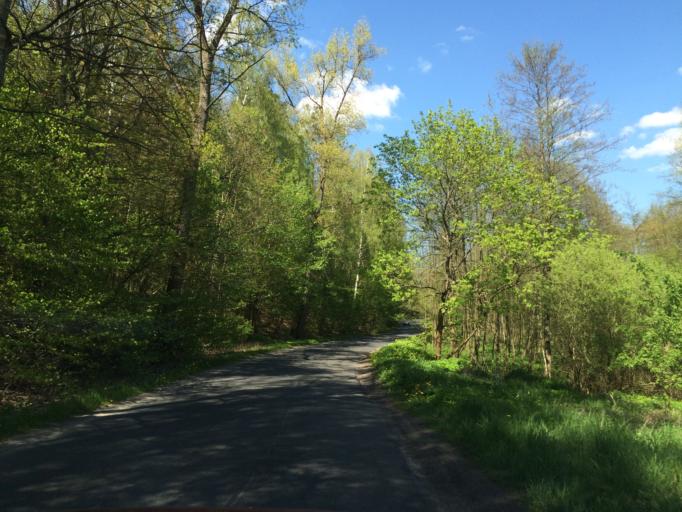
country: PL
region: Warmian-Masurian Voivodeship
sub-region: Powiat ilawski
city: Lubawa
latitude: 53.3990
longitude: 19.7456
